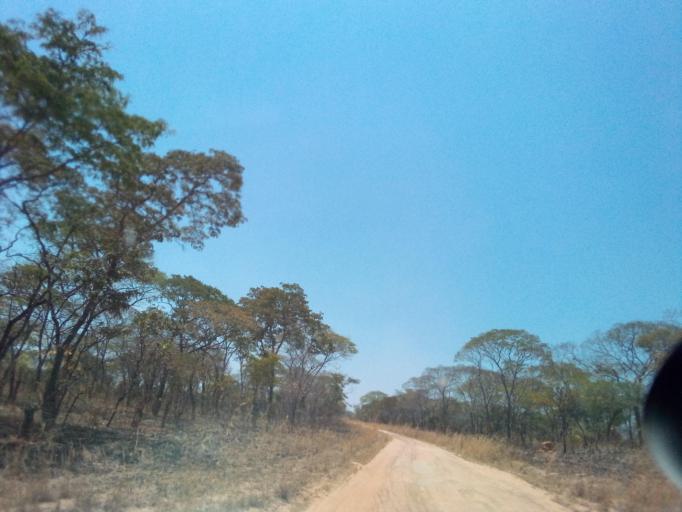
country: ZM
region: Northern
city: Mpika
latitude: -12.2535
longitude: 30.6946
